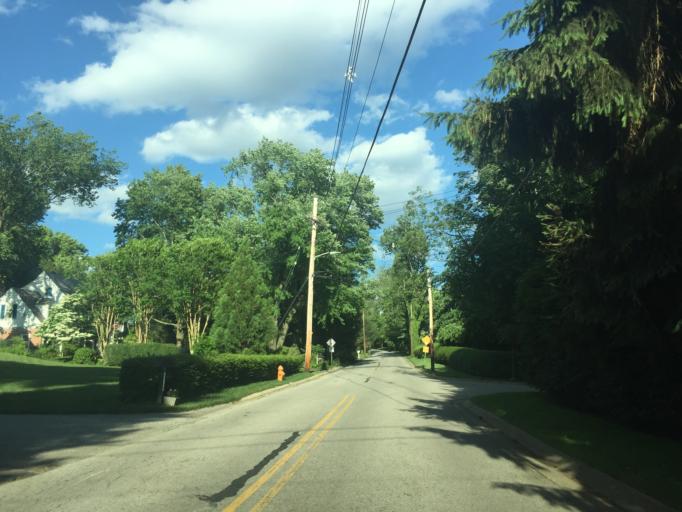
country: US
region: Maryland
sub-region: Baltimore County
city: Towson
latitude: 39.3685
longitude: -76.6382
